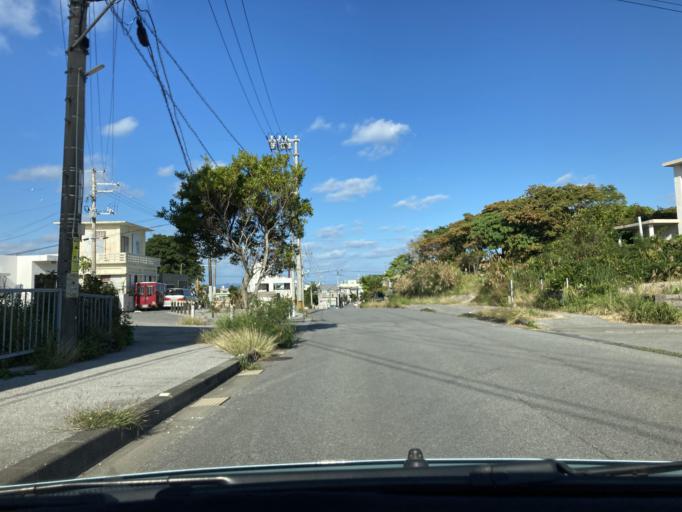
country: JP
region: Okinawa
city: Katsuren-haebaru
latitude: 26.3207
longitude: 127.9100
